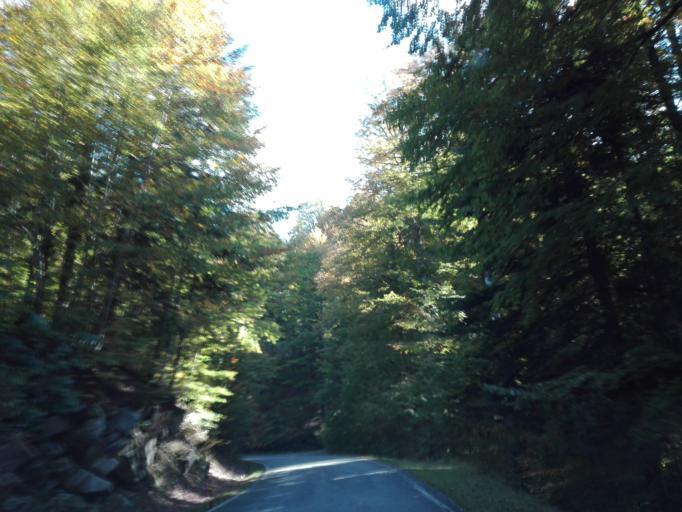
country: ES
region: Navarre
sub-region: Provincia de Navarra
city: Oronz
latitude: 42.9702
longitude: -1.1163
